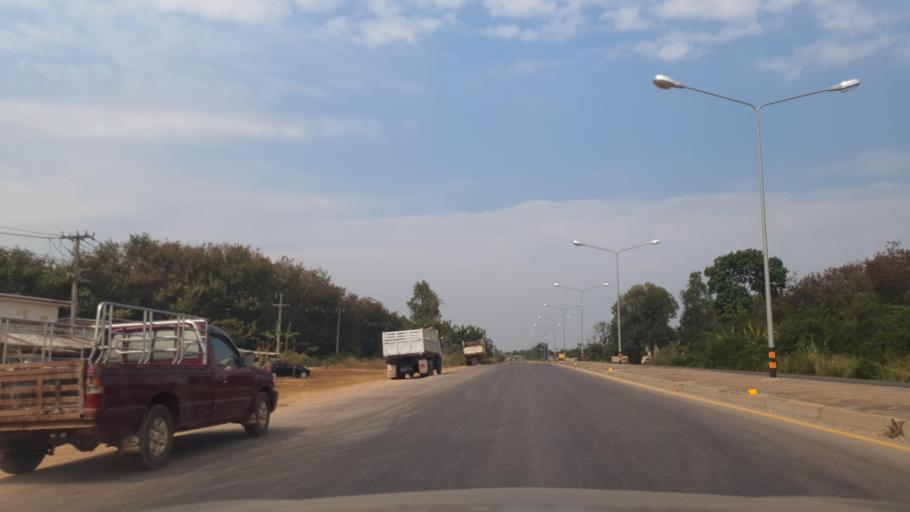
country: TH
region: Changwat Bueng Kan
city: Si Wilai
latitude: 18.2992
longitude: 103.8170
